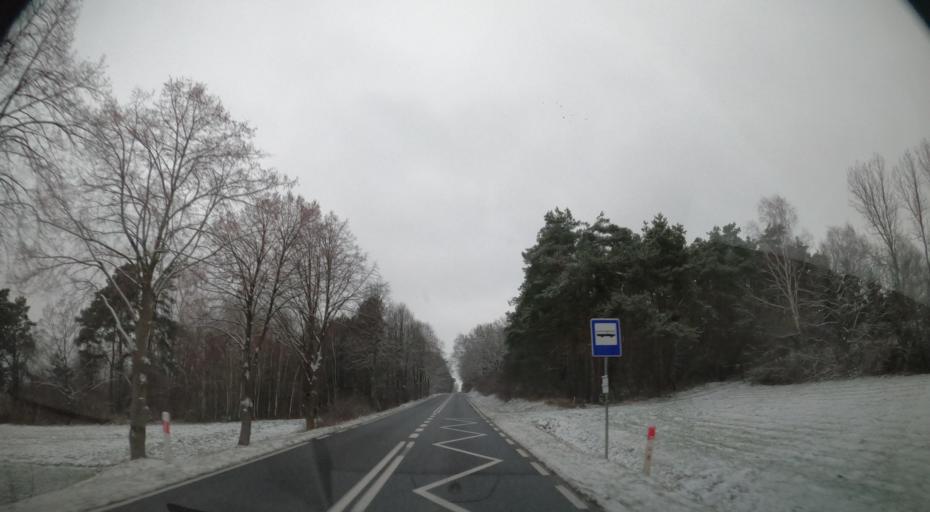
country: PL
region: Masovian Voivodeship
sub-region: Powiat plocki
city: Nowy Duninow
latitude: 52.5839
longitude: 19.5233
